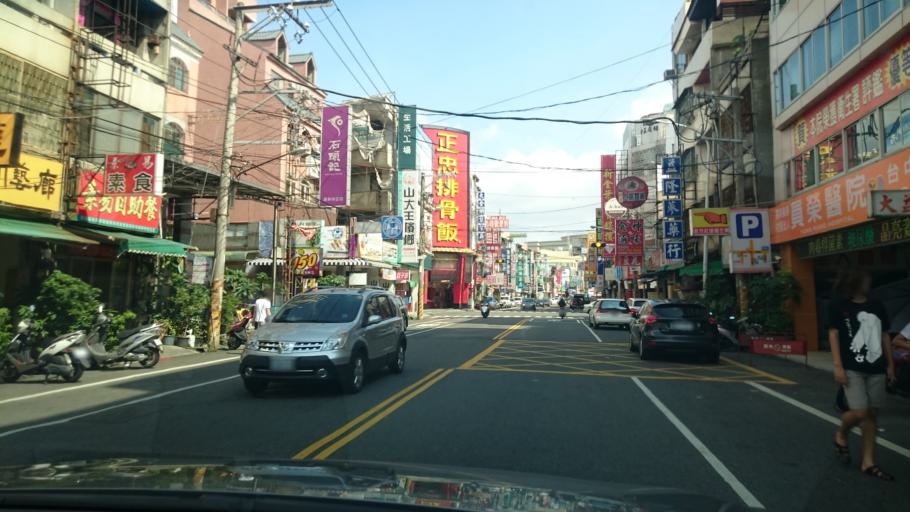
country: TW
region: Taiwan
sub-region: Nantou
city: Nantou
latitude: 23.9536
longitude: 120.5749
